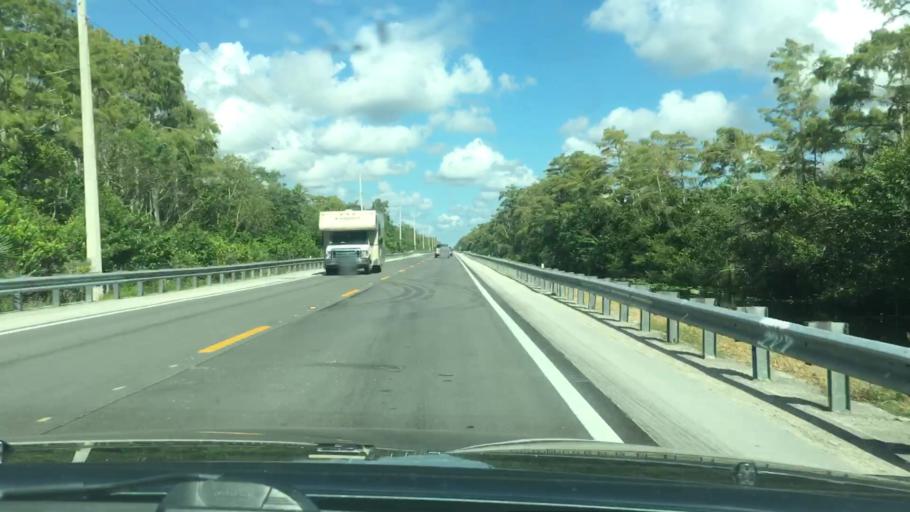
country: US
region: Florida
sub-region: Miami-Dade County
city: Kendall West
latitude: 25.7680
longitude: -80.8345
